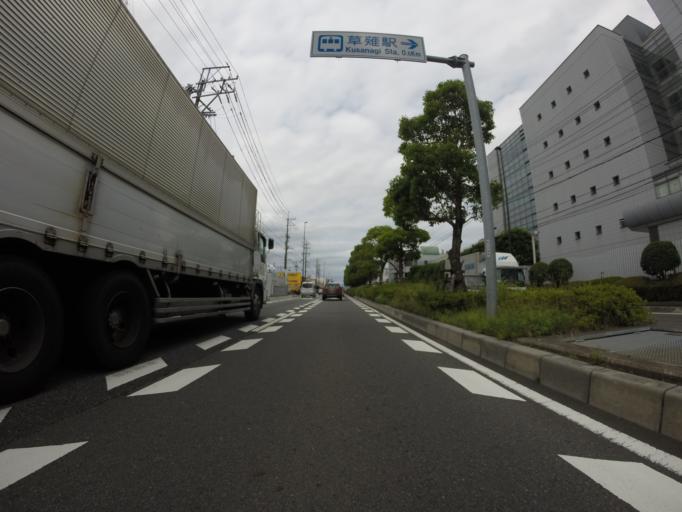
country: JP
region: Shizuoka
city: Shizuoka-shi
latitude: 35.0054
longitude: 138.4410
